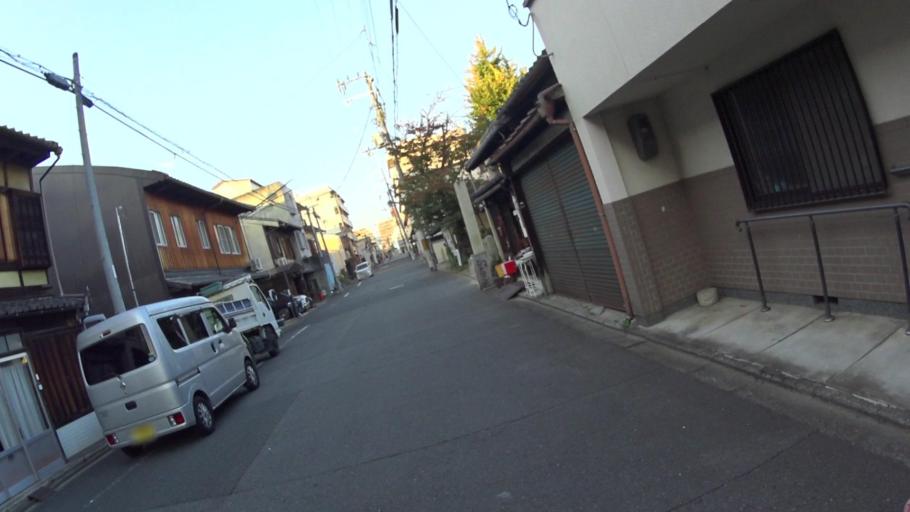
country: JP
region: Kyoto
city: Kyoto
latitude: 35.0256
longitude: 135.7489
